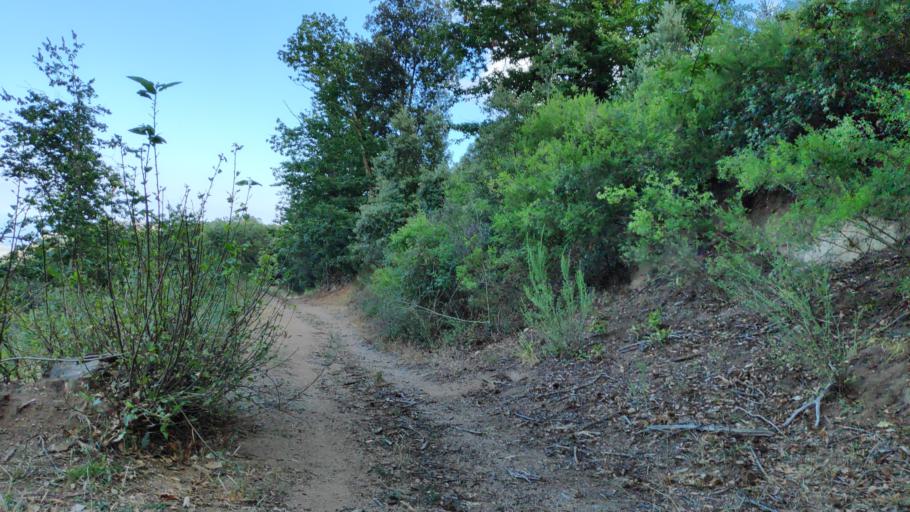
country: IT
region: Calabria
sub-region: Provincia di Reggio Calabria
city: Pazzano
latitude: 38.4727
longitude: 16.4131
